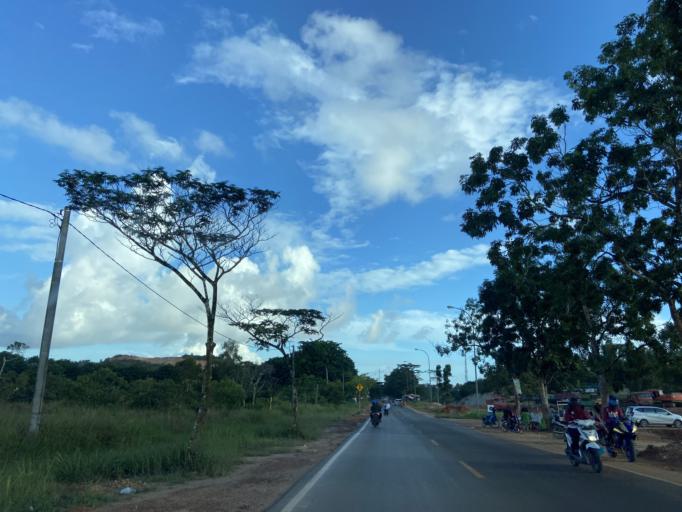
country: SG
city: Singapore
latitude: 1.0229
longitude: 104.0115
